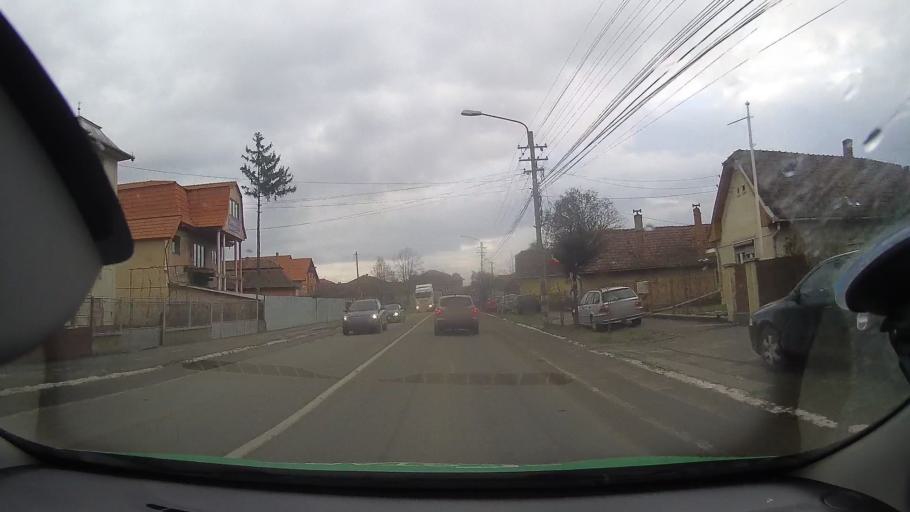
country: RO
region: Cluj
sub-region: Municipiul Campia Turzii
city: Campia Turzii
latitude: 46.5488
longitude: 23.8863
